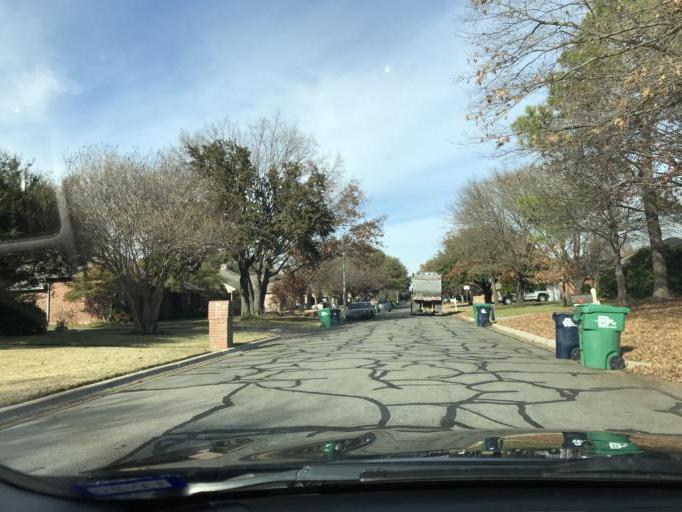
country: US
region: Texas
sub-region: Denton County
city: Denton
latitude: 33.2333
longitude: -97.1525
